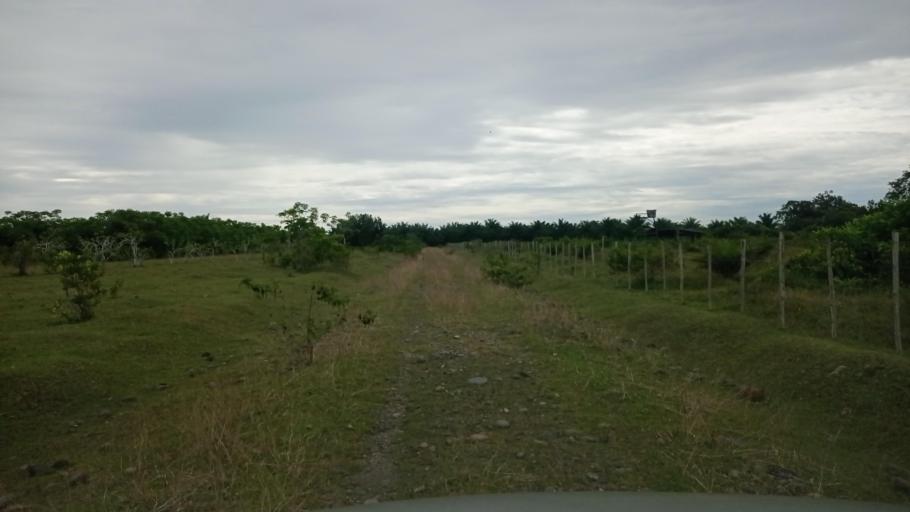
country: ID
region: Jambi
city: Sungai Penuh
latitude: -2.5156
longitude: 101.0621
